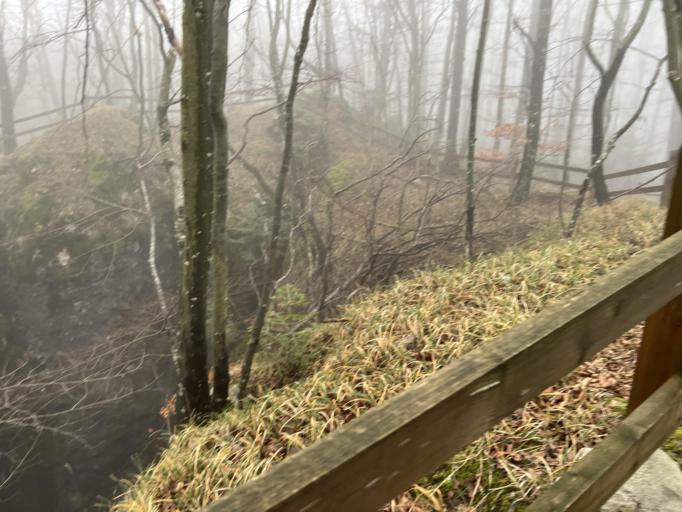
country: SI
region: Nova Gorica
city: Sempas
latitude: 45.9805
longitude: 13.7557
